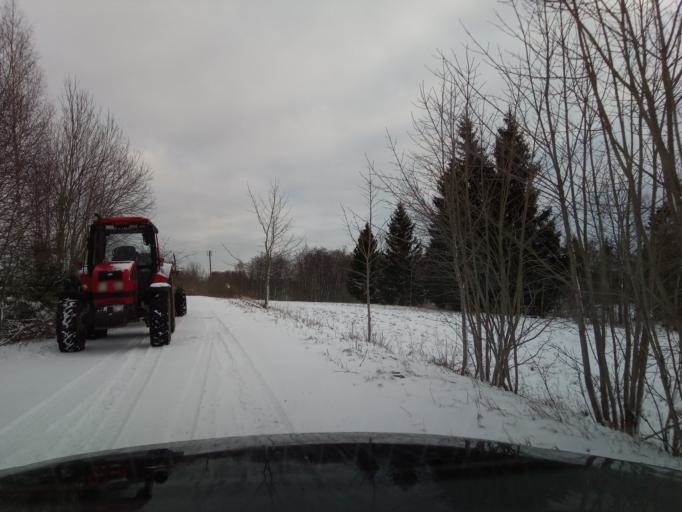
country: LT
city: Zarasai
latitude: 55.7300
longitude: 25.9511
